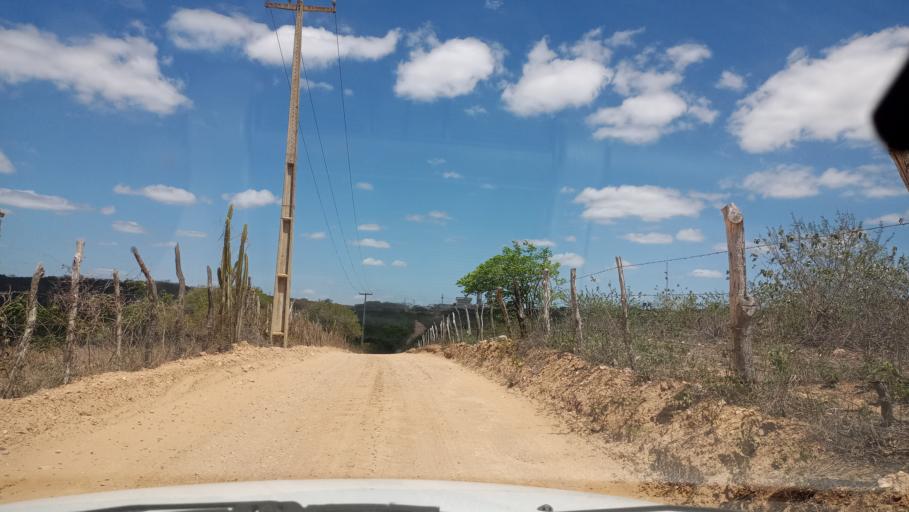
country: BR
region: Rio Grande do Norte
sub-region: Sao Paulo Do Potengi
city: Sao Paulo do Potengi
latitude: -5.7943
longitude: -35.9215
